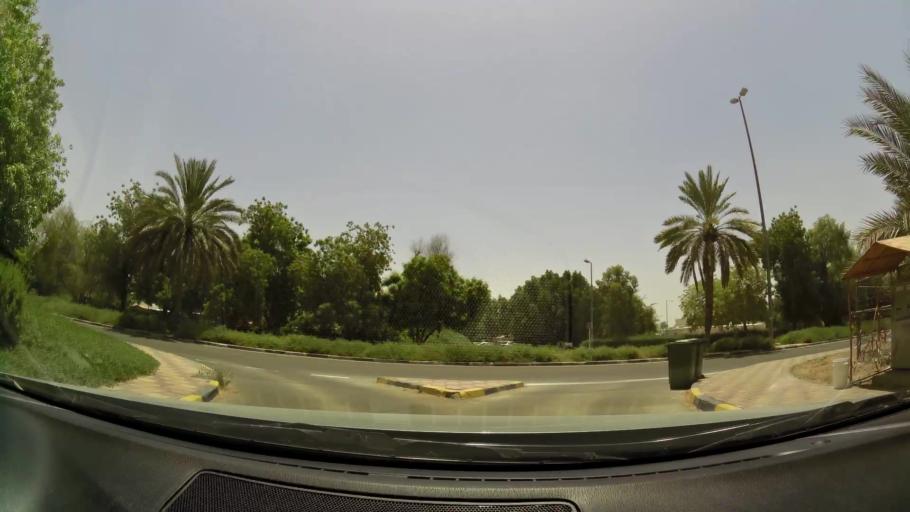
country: OM
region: Al Buraimi
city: Al Buraymi
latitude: 24.2712
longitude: 55.7405
